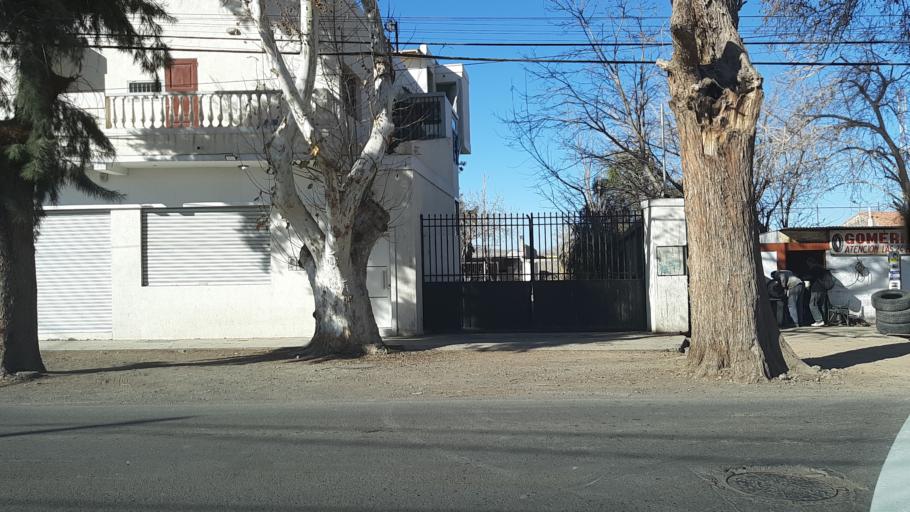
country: AR
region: San Juan
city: San Juan
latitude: -31.5401
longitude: -68.5671
